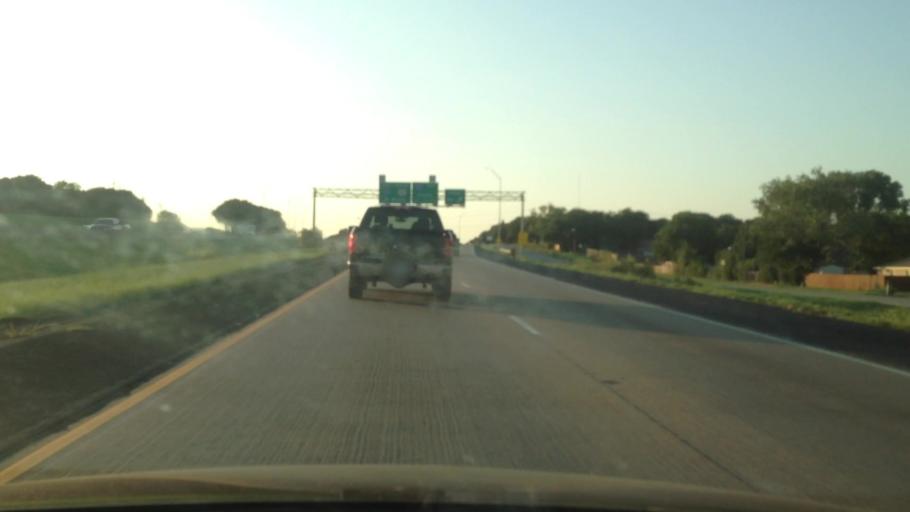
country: US
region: Texas
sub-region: Tarrant County
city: Kennedale
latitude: 32.6628
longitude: -97.1989
